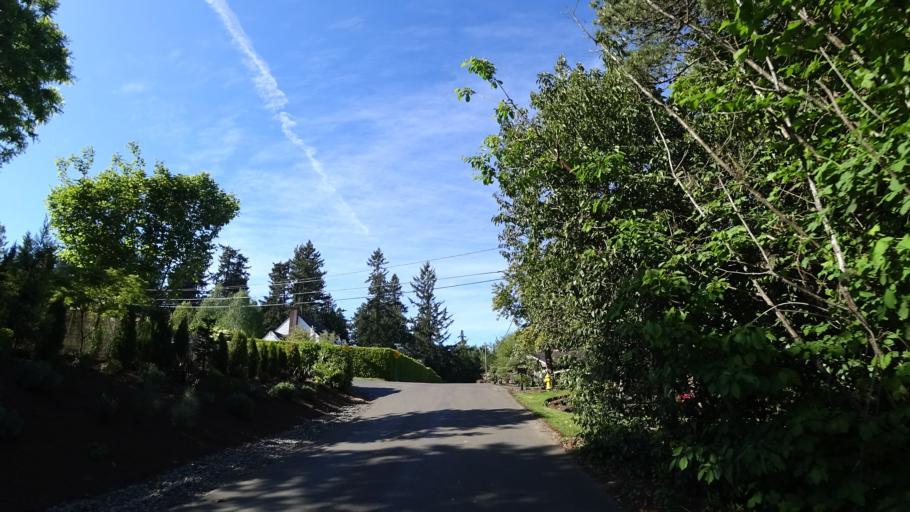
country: US
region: Oregon
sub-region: Washington County
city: Raleigh Hills
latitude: 45.4874
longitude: -122.7490
